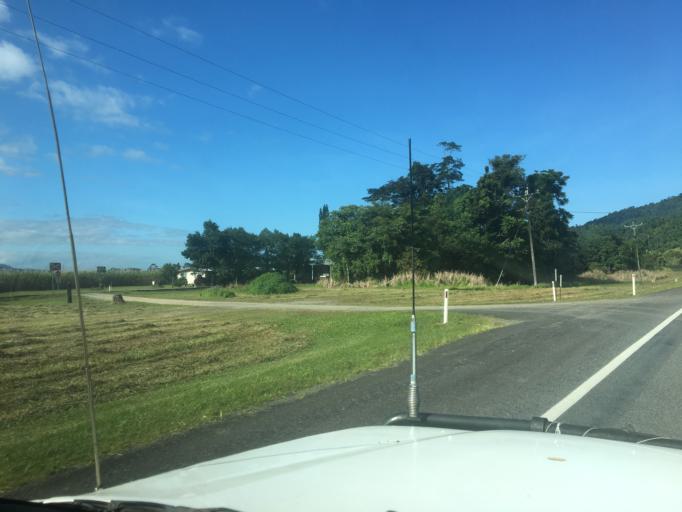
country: AU
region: Queensland
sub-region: Cassowary Coast
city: Innisfail
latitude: -17.3067
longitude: 145.9271
